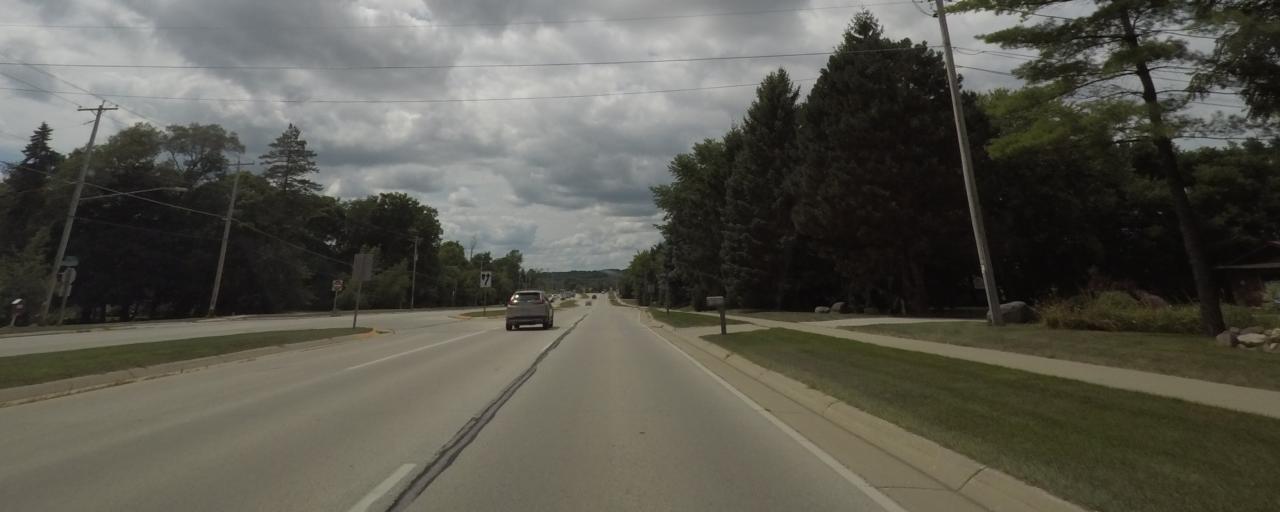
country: US
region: Wisconsin
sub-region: Waukesha County
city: New Berlin
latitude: 43.0172
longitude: -88.1578
